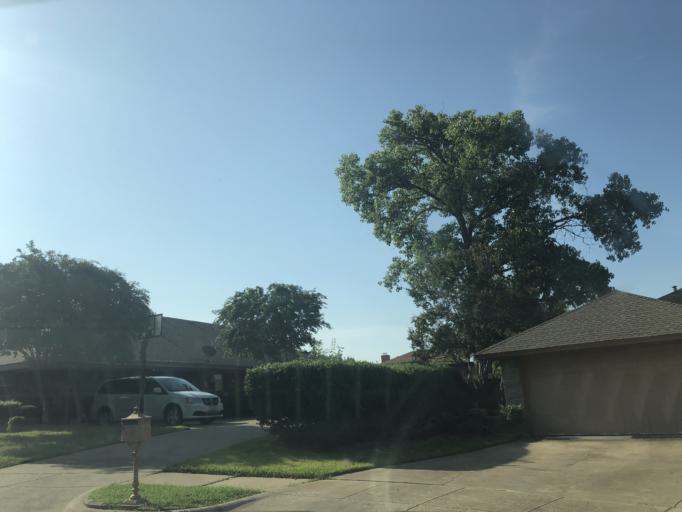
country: US
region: Texas
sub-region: Tarrant County
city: Euless
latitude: 32.8733
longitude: -97.0912
